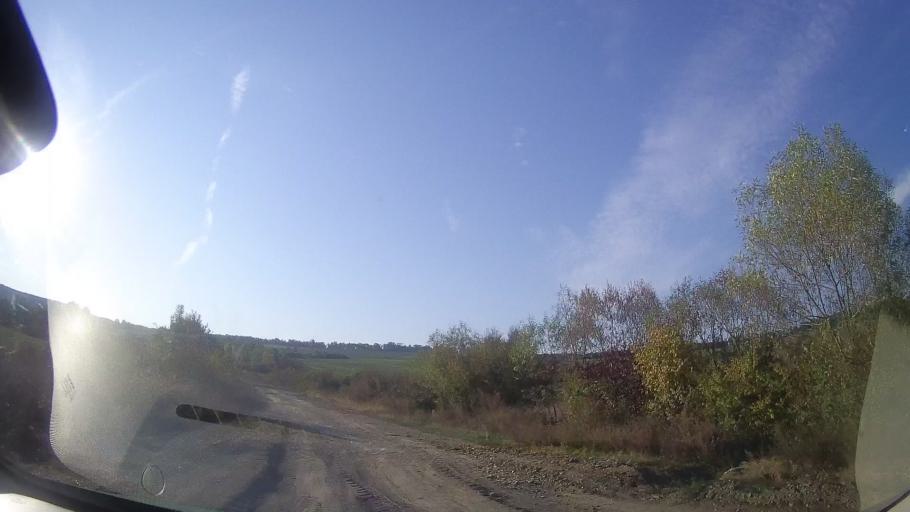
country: RO
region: Timis
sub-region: Comuna Bogda
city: Bogda
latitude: 45.9531
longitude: 21.6146
